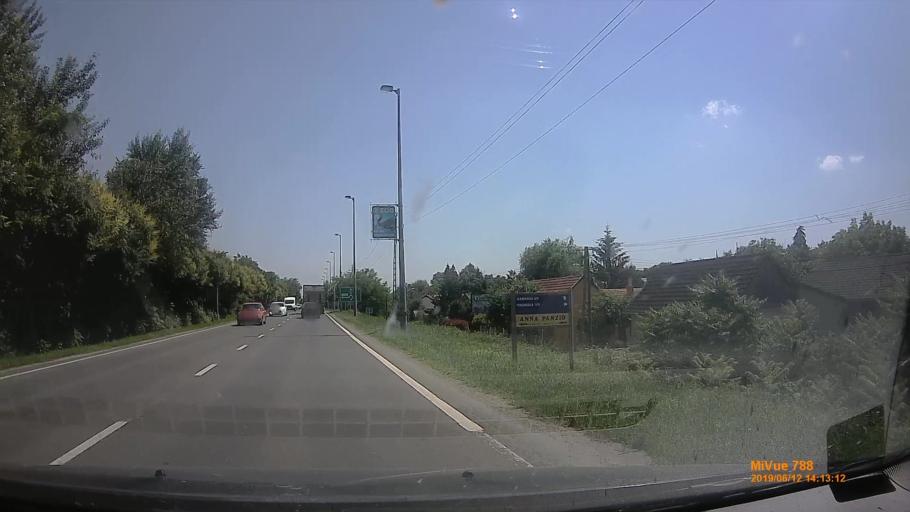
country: HU
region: Csongrad
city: Szeged
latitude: 46.2343
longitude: 20.1727
